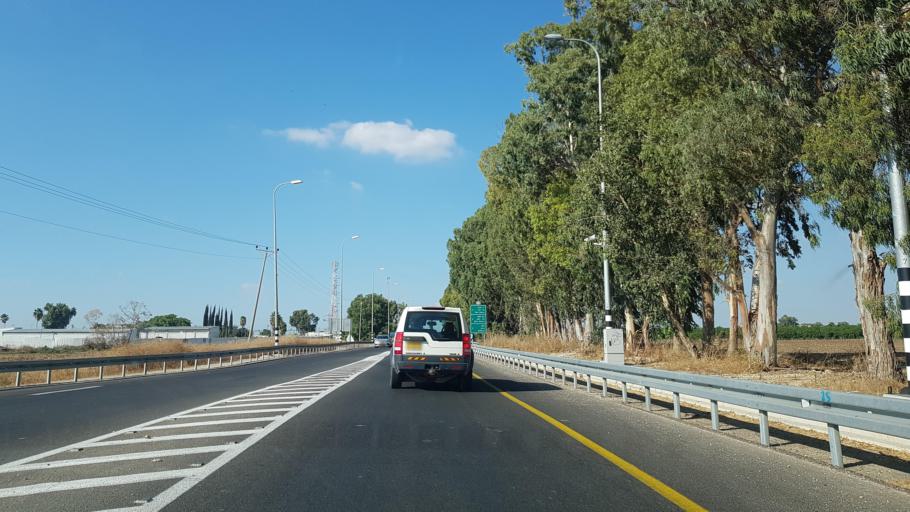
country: PS
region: West Bank
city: Tulkarm
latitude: 32.3129
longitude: 34.9993
